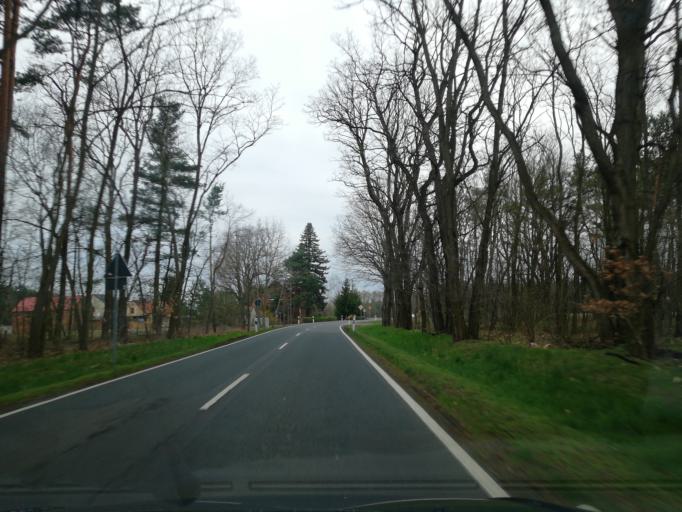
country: DE
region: Brandenburg
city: Vetschau
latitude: 51.7383
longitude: 14.0537
